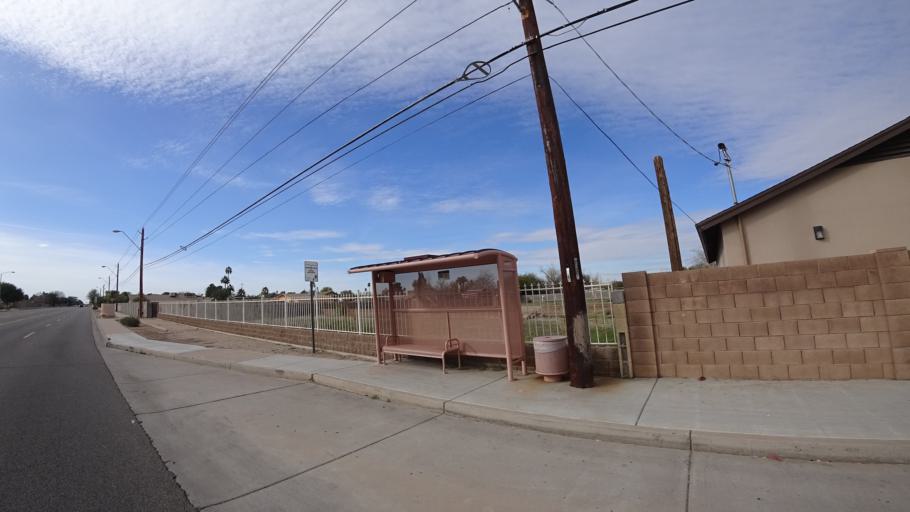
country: US
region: Arizona
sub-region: Maricopa County
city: Glendale
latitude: 33.6319
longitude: -112.1512
